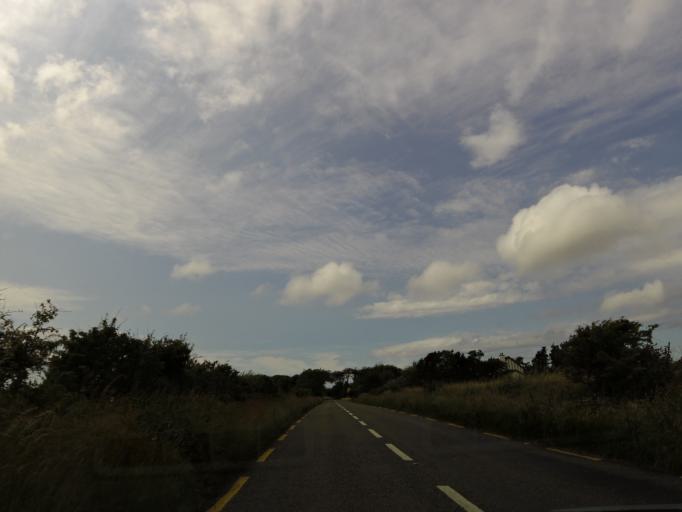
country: IE
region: Munster
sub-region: An Clar
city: Kilrush
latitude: 52.6737
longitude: -9.6024
